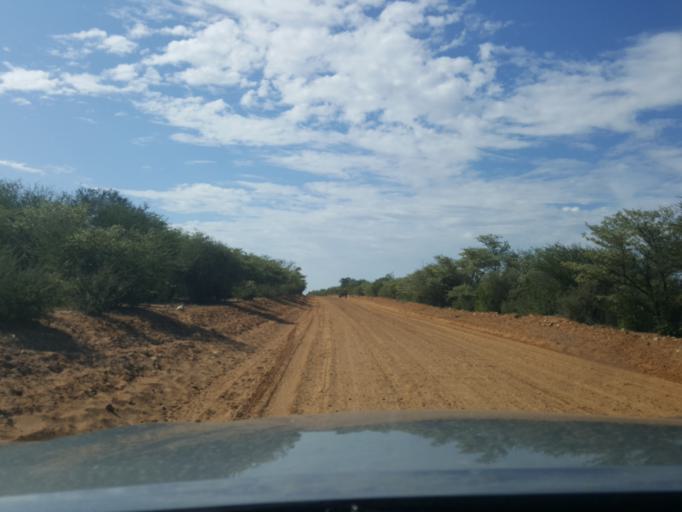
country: BW
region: Kweneng
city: Khudumelapye
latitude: -23.6378
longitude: 24.7298
